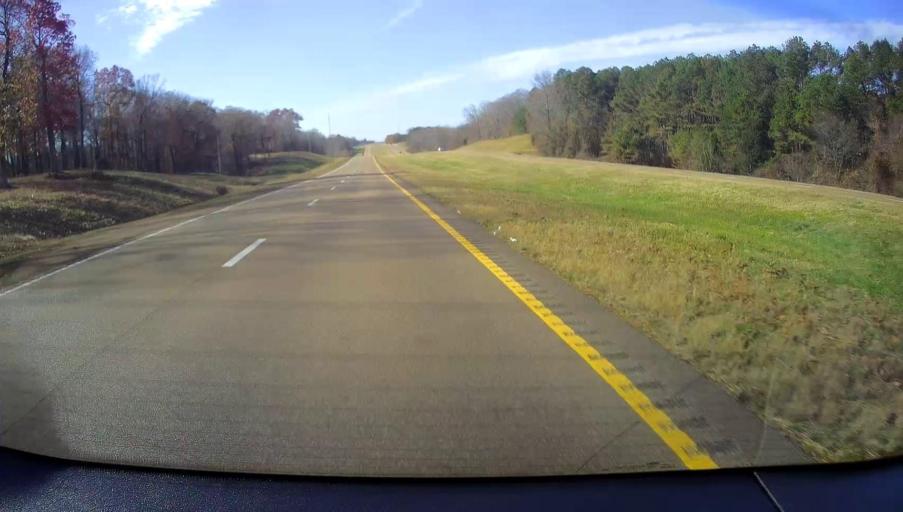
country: US
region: Mississippi
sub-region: Benton County
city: Ashland
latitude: 34.9473
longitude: -89.1205
